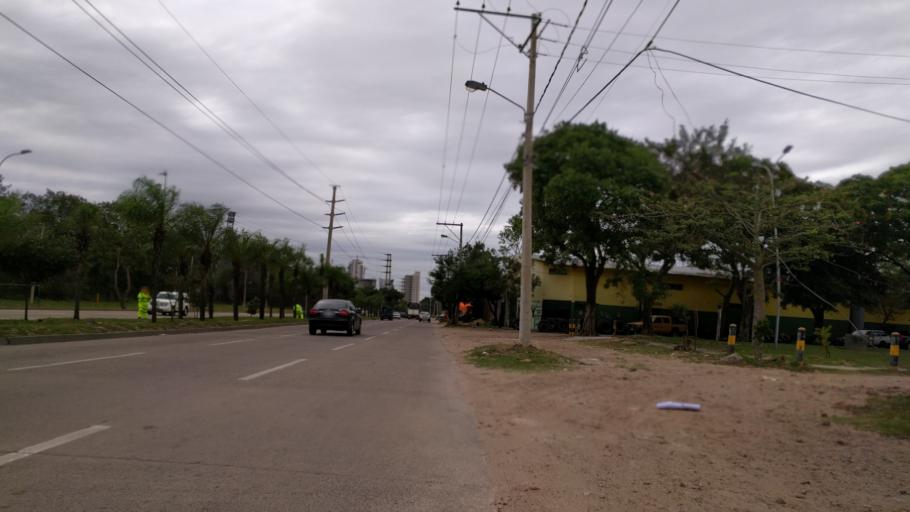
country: BO
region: Santa Cruz
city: Santa Cruz de la Sierra
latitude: -17.7700
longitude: -63.2093
